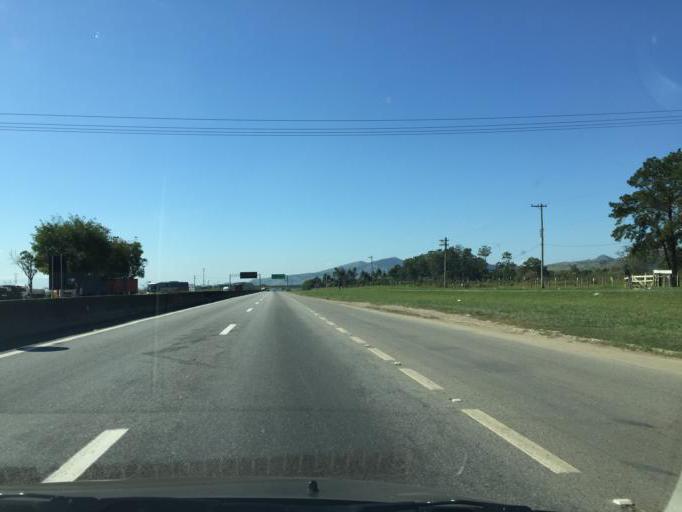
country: BR
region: Sao Paulo
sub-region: Pindamonhangaba
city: Pindamonhangaba
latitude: -22.9256
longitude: -45.3516
